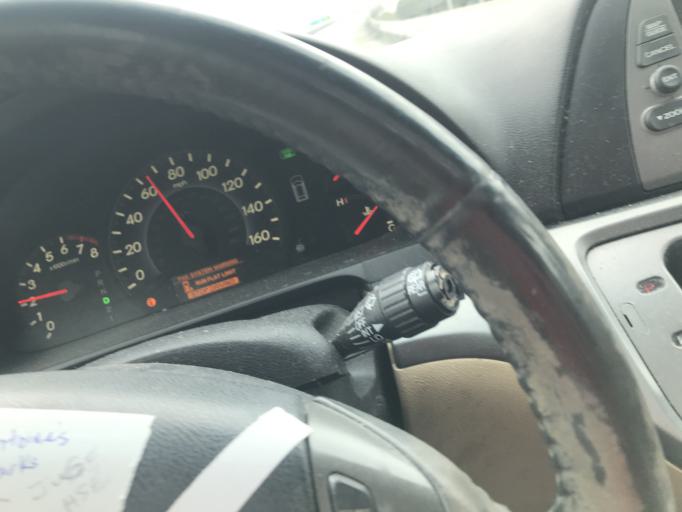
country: US
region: Louisiana
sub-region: Jefferson Parish
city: Gretna
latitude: 29.9336
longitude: -90.0390
